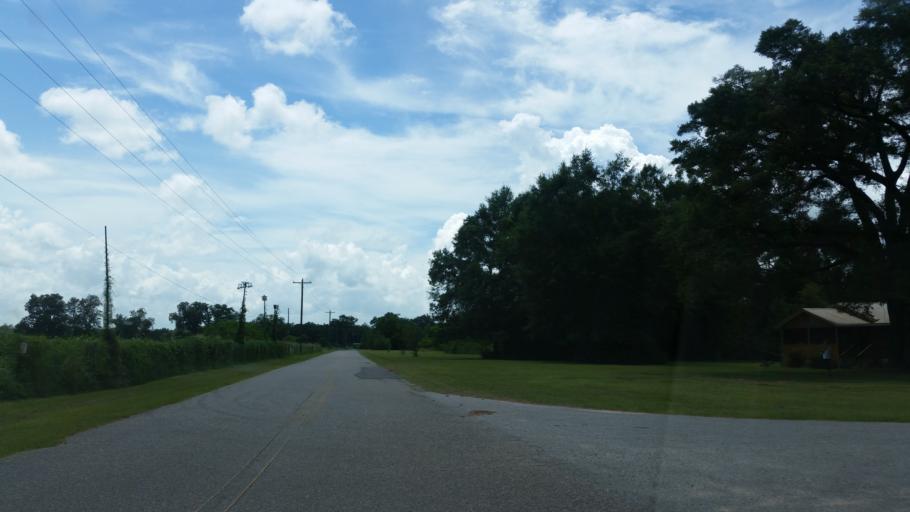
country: US
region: Florida
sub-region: Okaloosa County
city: Crestview
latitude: 30.7333
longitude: -86.8088
